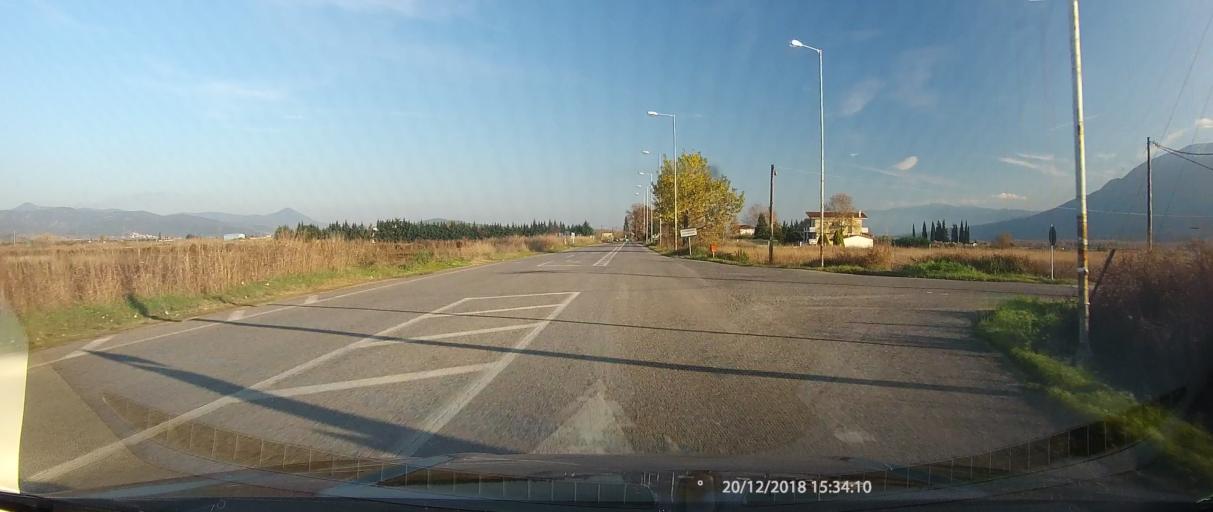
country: GR
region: Central Greece
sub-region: Nomos Fthiotidos
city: Lianokladhion
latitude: 38.9200
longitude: 22.2906
